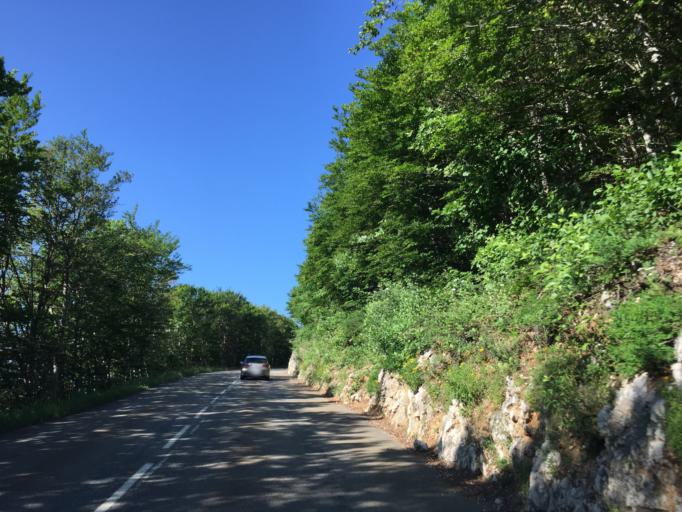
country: FR
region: Rhone-Alpes
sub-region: Departement de la Drome
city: Saint-Laurent-en-Royans
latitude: 44.9162
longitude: 5.3704
